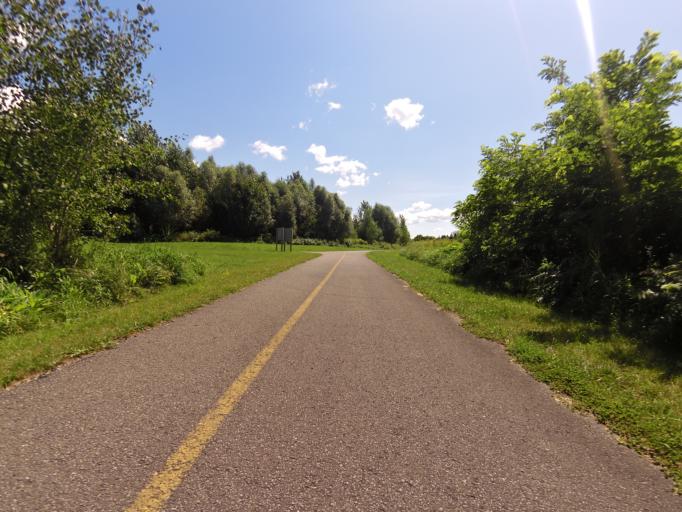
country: CA
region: Ontario
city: Ottawa
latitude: 45.3608
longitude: -75.6630
